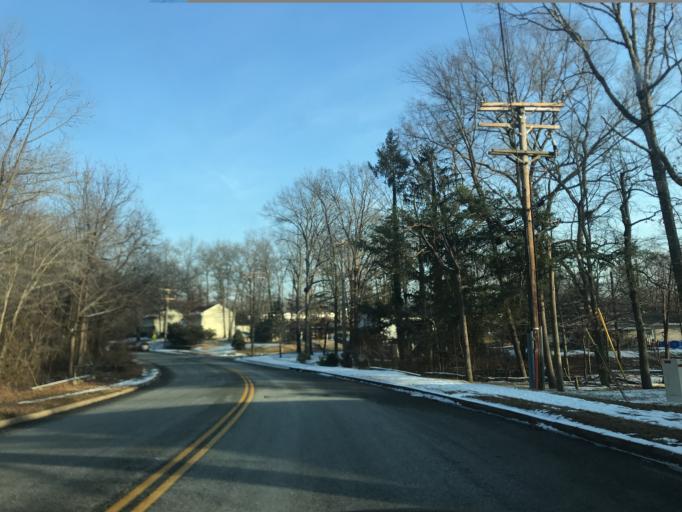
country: US
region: Maryland
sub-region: Harford County
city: Joppatowne
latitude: 39.4216
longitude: -76.3651
